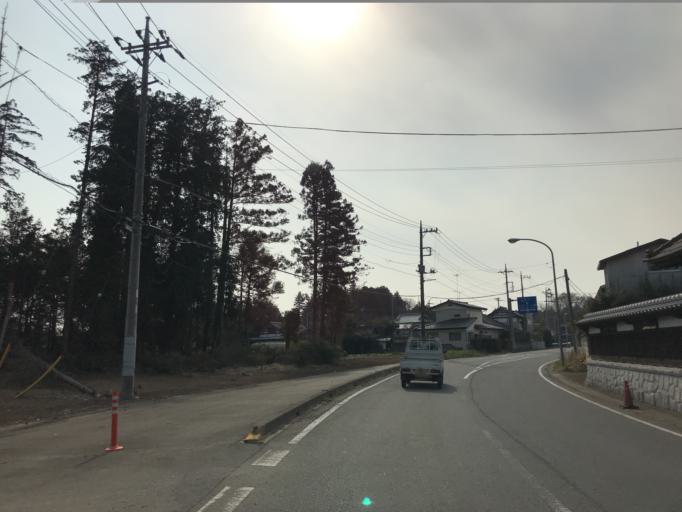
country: JP
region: Ibaraki
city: Okunoya
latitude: 36.2341
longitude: 140.3786
